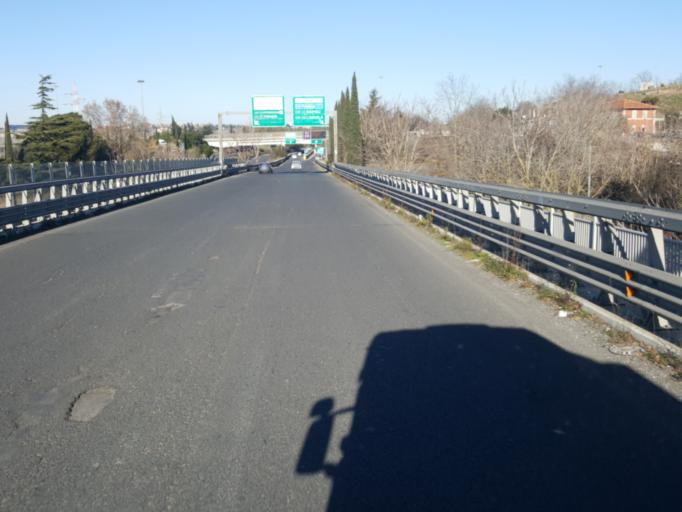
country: IT
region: Latium
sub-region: Citta metropolitana di Roma Capitale
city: Vitinia
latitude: 41.8038
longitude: 12.4194
